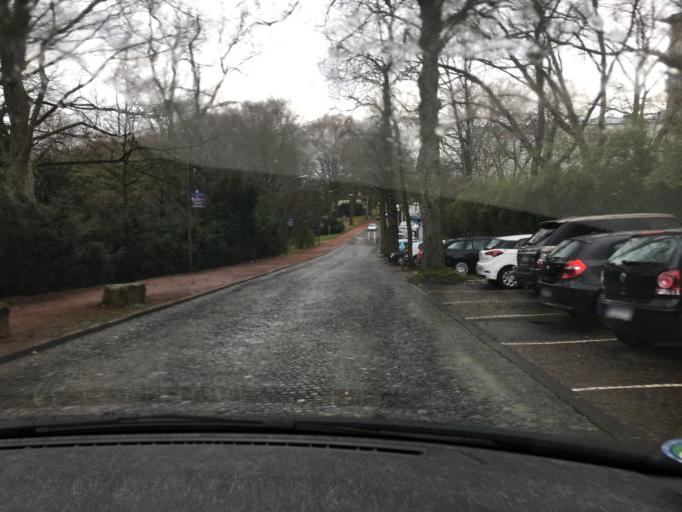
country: DE
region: North Rhine-Westphalia
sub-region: Regierungsbezirk Arnsberg
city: Bochum
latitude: 51.4921
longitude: 7.2279
